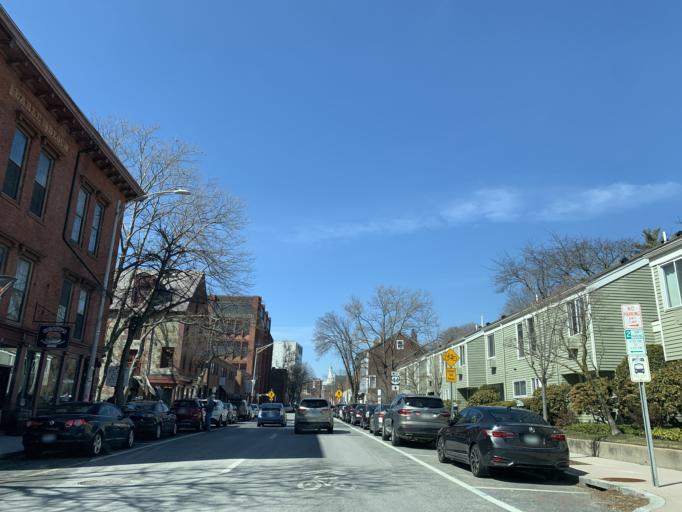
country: US
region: Rhode Island
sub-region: Providence County
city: Providence
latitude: 41.8208
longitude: -71.4037
